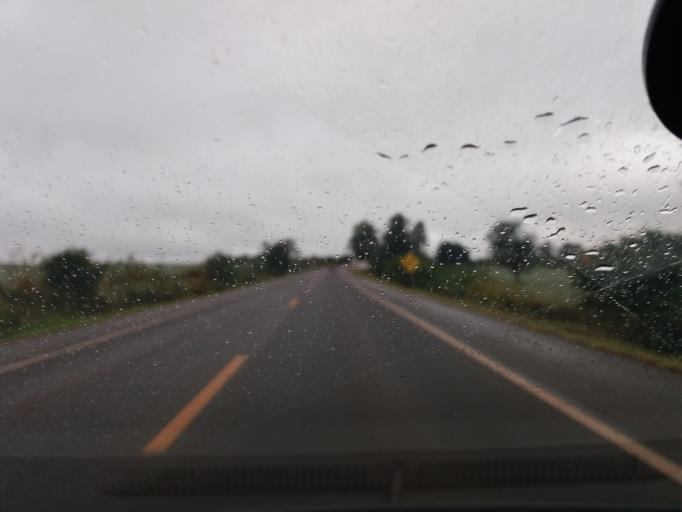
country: BR
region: Parana
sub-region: Moreira Sales
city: Moreira Sales
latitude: -24.3347
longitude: -52.6903
